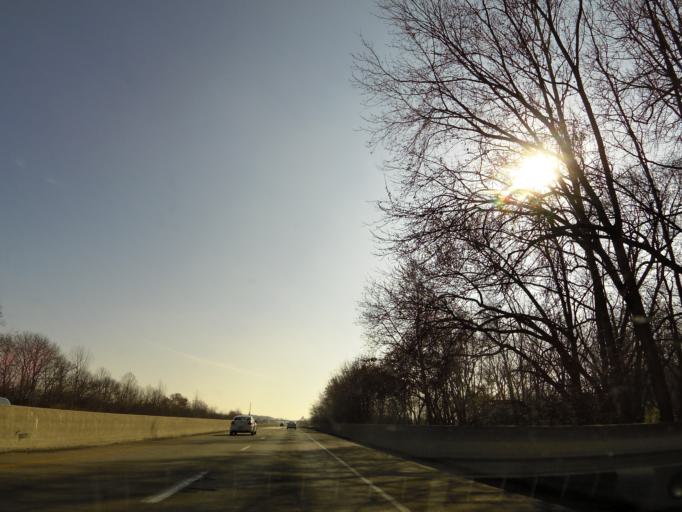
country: US
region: Indiana
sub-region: Shelby County
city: Shelbyville
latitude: 39.5919
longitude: -85.8339
